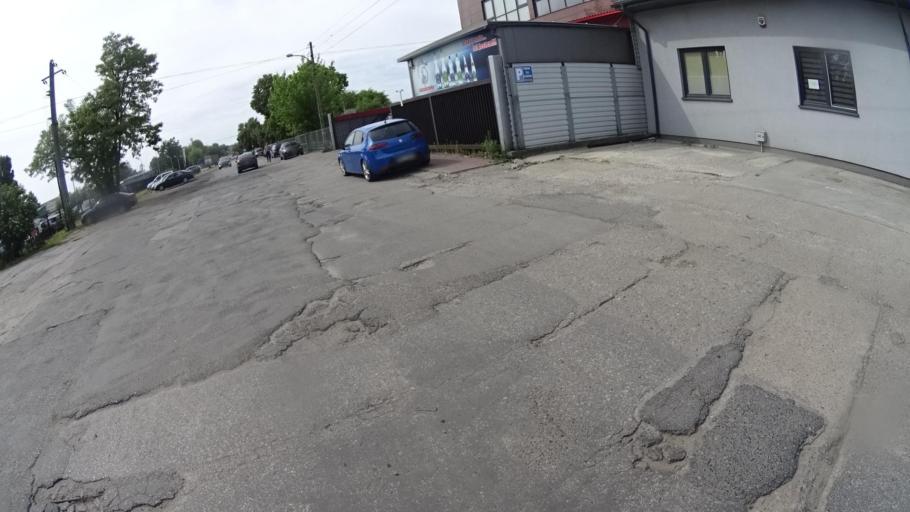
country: PL
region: Masovian Voivodeship
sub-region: Warszawa
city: Wlochy
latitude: 52.1892
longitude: 20.9416
